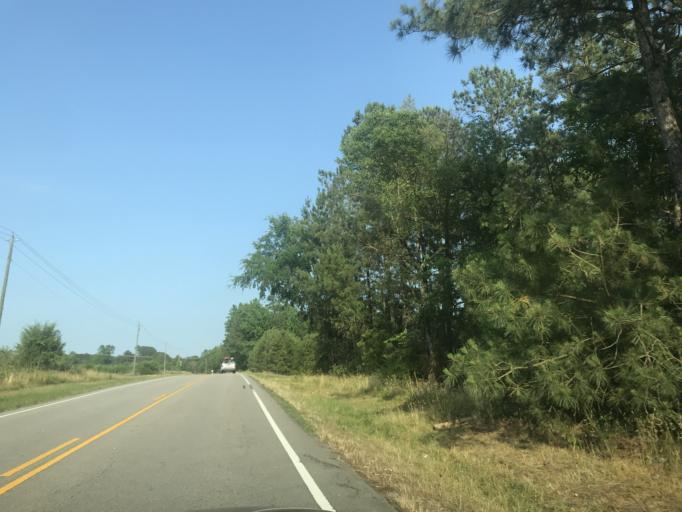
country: US
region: North Carolina
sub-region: Wake County
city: Rolesville
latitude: 35.8613
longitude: -78.4726
